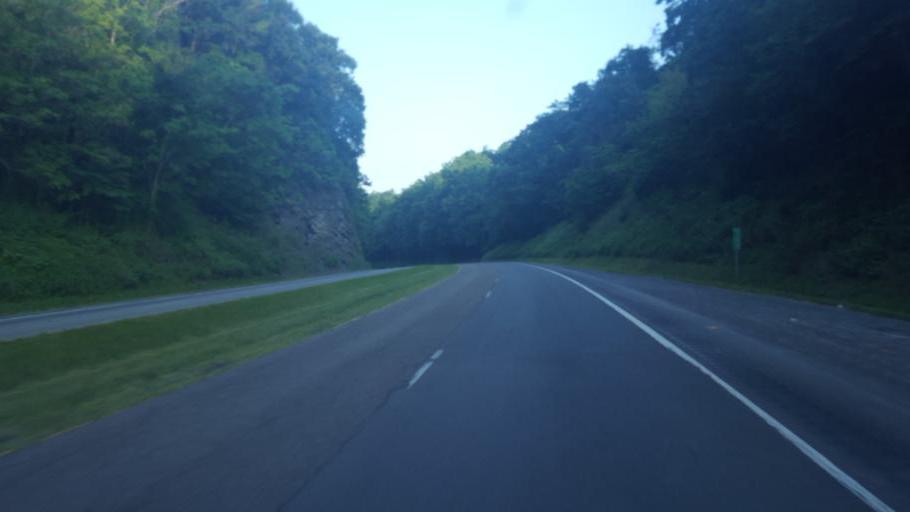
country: US
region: Virginia
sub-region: Wise County
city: Big Stone Gap
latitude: 36.7022
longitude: -82.7746
